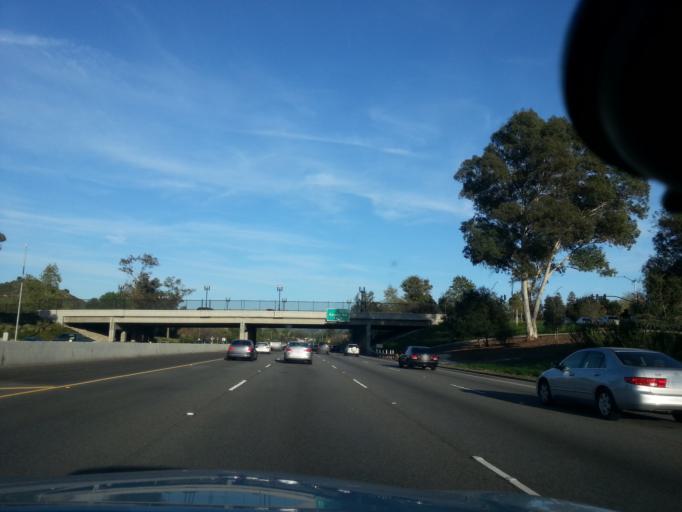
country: US
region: California
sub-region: Los Angeles County
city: Agoura Hills
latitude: 34.1467
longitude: -118.7825
